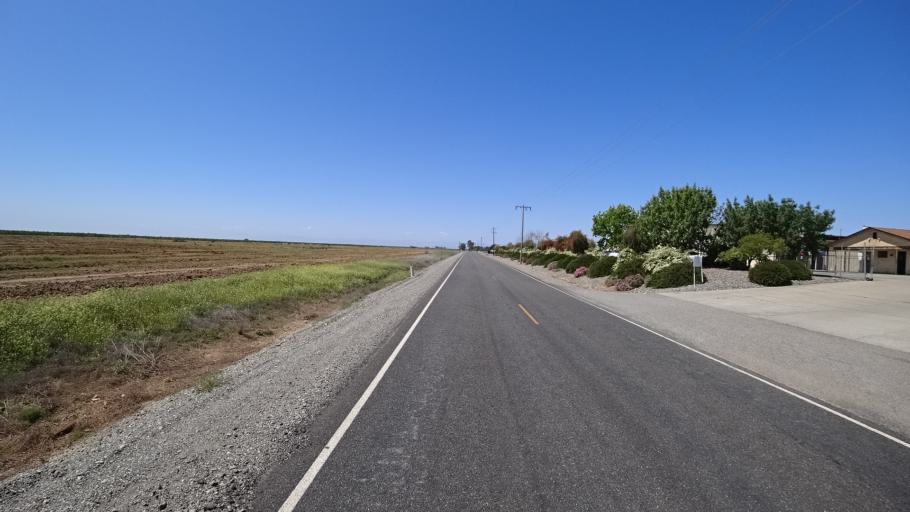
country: US
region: California
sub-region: Glenn County
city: Hamilton City
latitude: 39.7665
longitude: -122.0610
